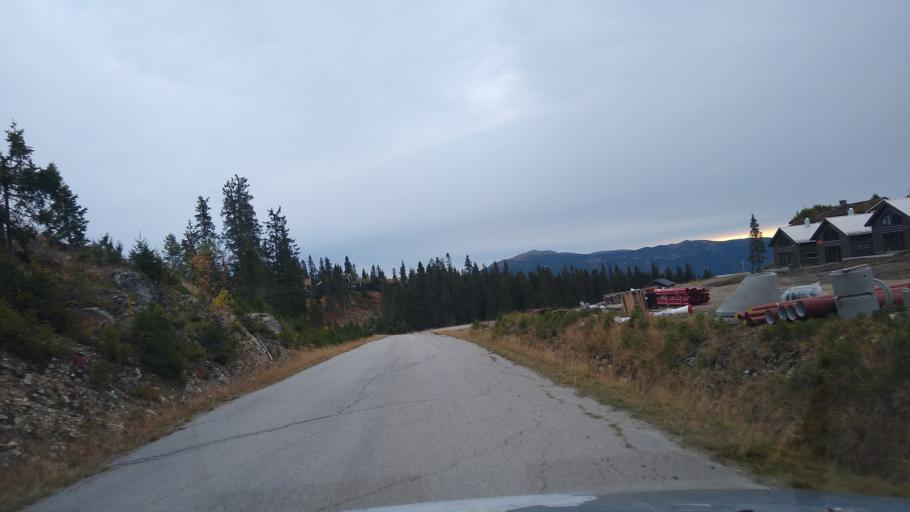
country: NO
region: Oppland
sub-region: Ringebu
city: Ringebu
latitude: 61.4736
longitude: 10.1311
